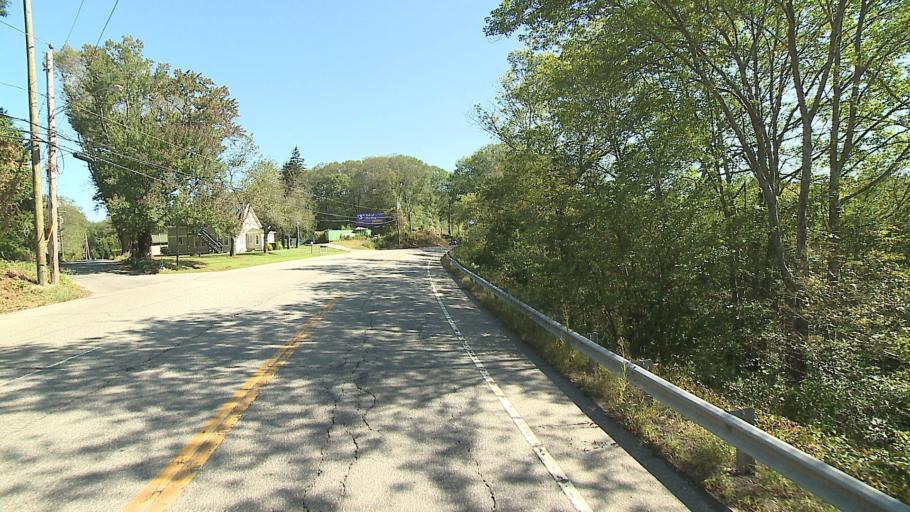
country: US
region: Connecticut
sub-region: New London County
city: Jewett City
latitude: 41.6291
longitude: -71.9667
